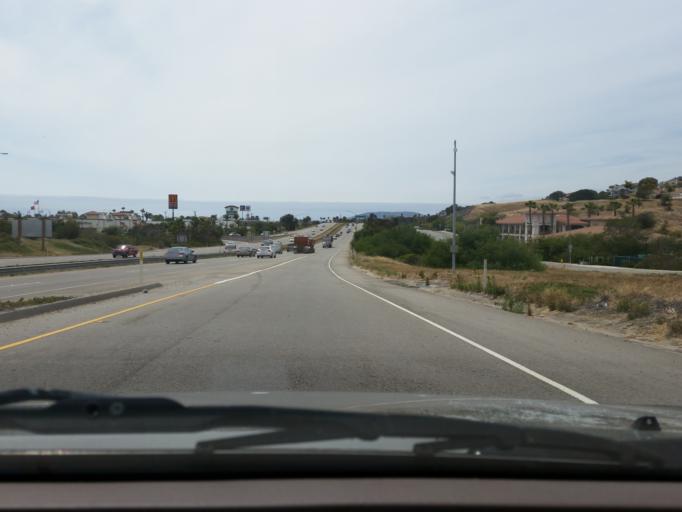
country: US
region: California
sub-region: San Luis Obispo County
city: Grover Beach
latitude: 35.1369
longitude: -120.6233
